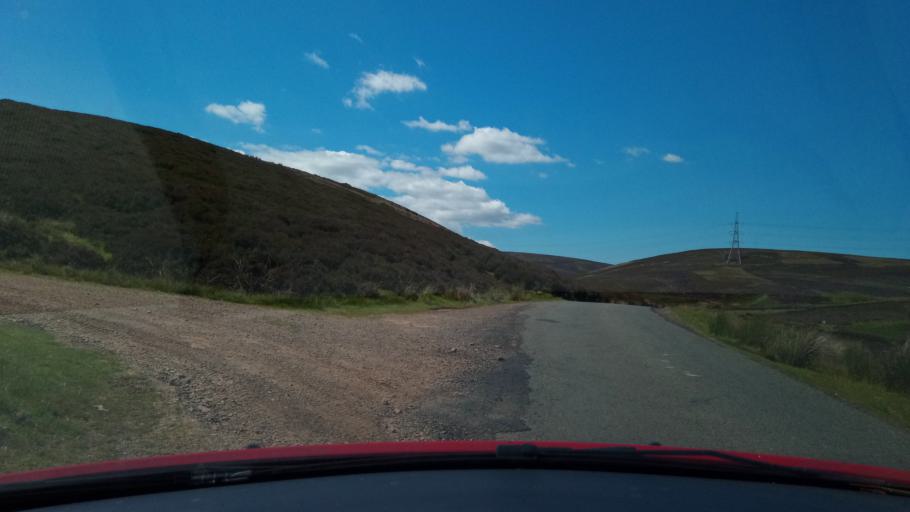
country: GB
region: Scotland
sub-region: East Lothian
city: East Linton
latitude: 55.8506
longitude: -2.5961
